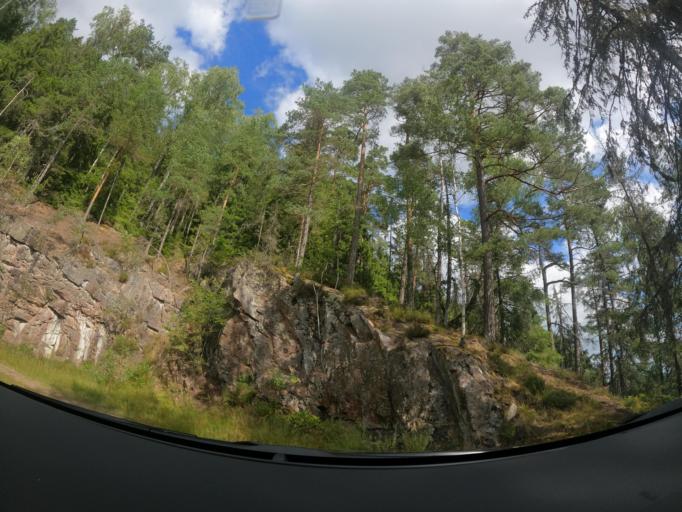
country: SE
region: Joenkoeping
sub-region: Gnosjo Kommun
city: Gnosjoe
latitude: 57.4296
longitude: 13.6132
